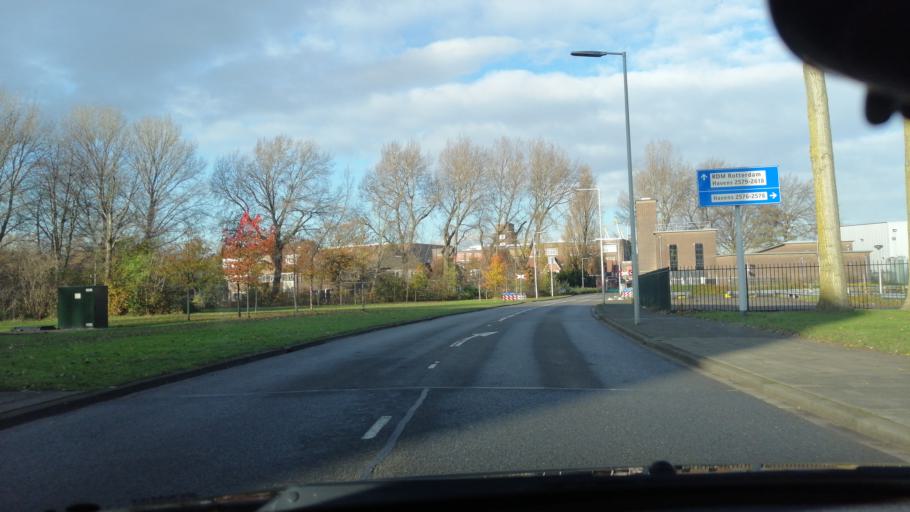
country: NL
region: South Holland
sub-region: Gemeente Rotterdam
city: Delfshaven
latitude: 51.8948
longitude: 4.4229
